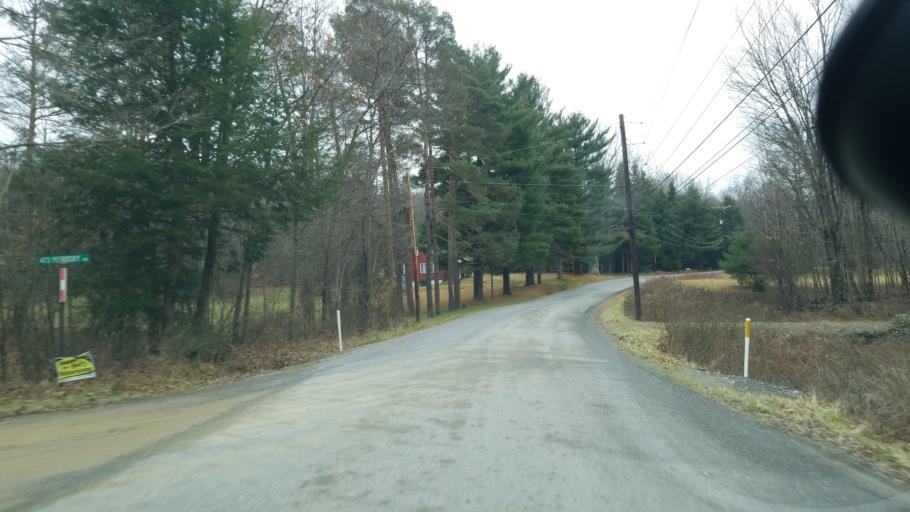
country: US
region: Pennsylvania
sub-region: Clearfield County
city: Treasure Lake
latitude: 41.1145
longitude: -78.6910
